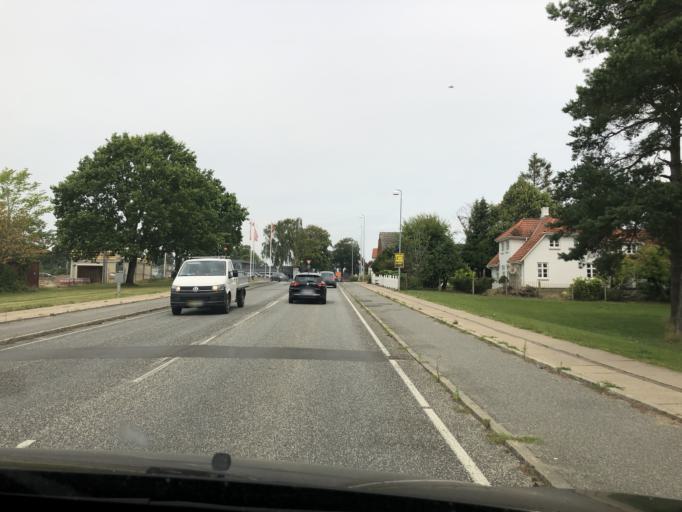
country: DK
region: South Denmark
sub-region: Assens Kommune
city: Glamsbjerg
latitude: 55.2721
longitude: 10.1083
